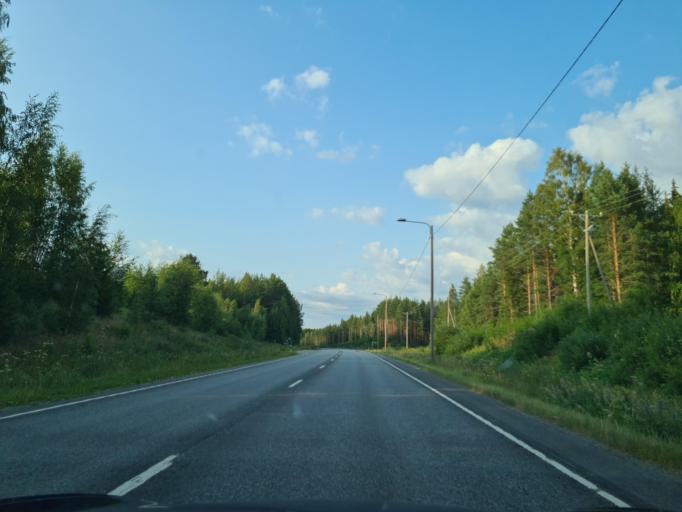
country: FI
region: Southern Ostrobothnia
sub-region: Seinaejoki
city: Kauhava
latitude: 63.0718
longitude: 23.0519
